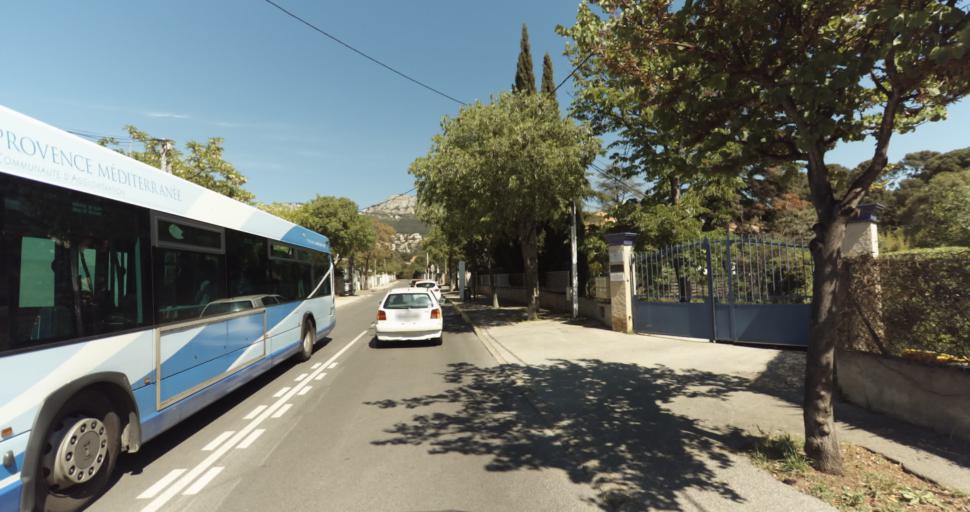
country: FR
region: Provence-Alpes-Cote d'Azur
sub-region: Departement du Var
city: Toulon
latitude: 43.1399
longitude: 5.9038
